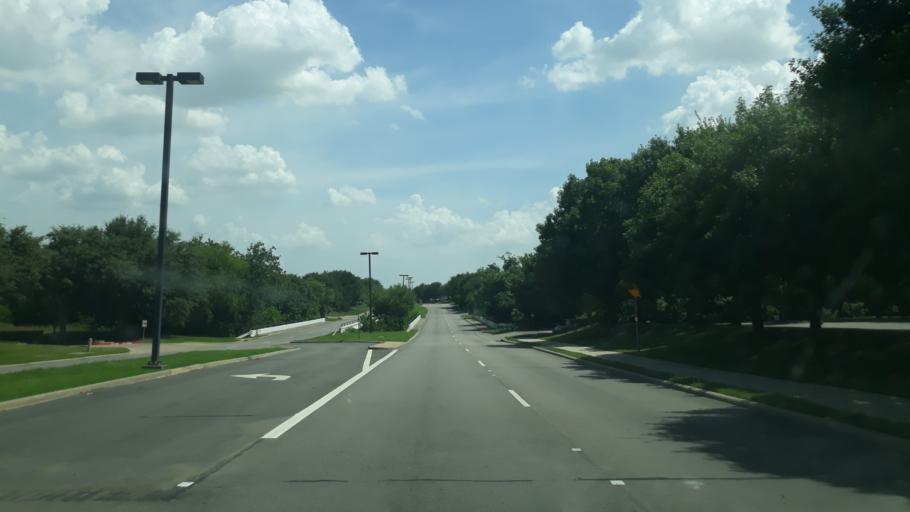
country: US
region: Texas
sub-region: Dallas County
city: Coppell
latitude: 32.9638
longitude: -97.0267
